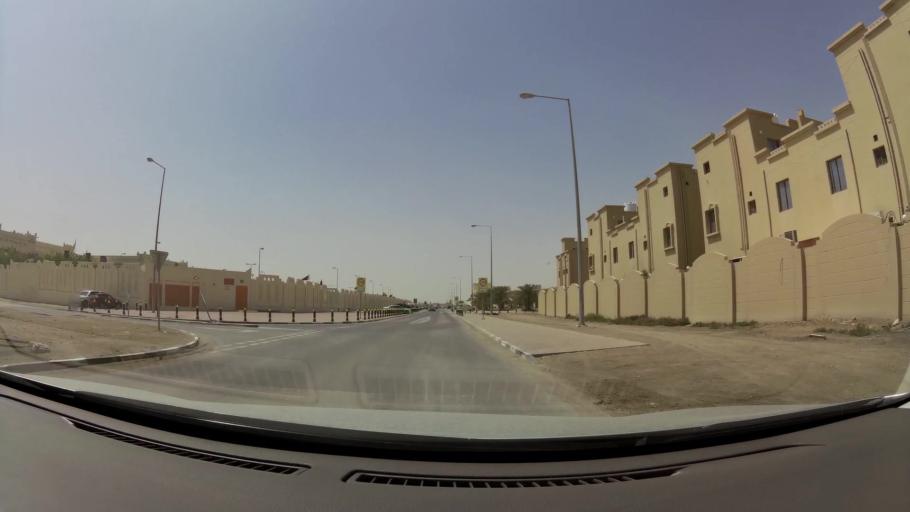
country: QA
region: Baladiyat Umm Salal
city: Umm Salal Muhammad
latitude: 25.3999
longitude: 51.4513
